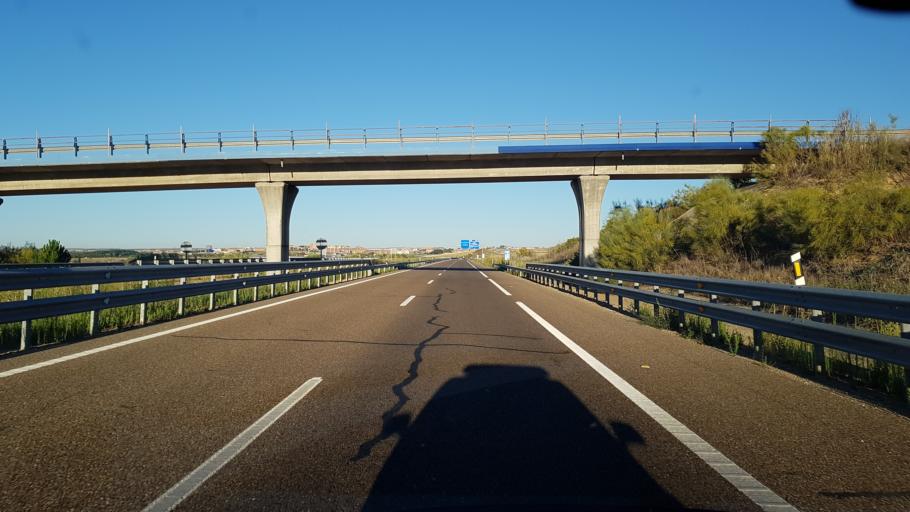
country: ES
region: Castille and Leon
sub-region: Provincia de Zamora
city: Monfarracinos
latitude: 41.5342
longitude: -5.6889
